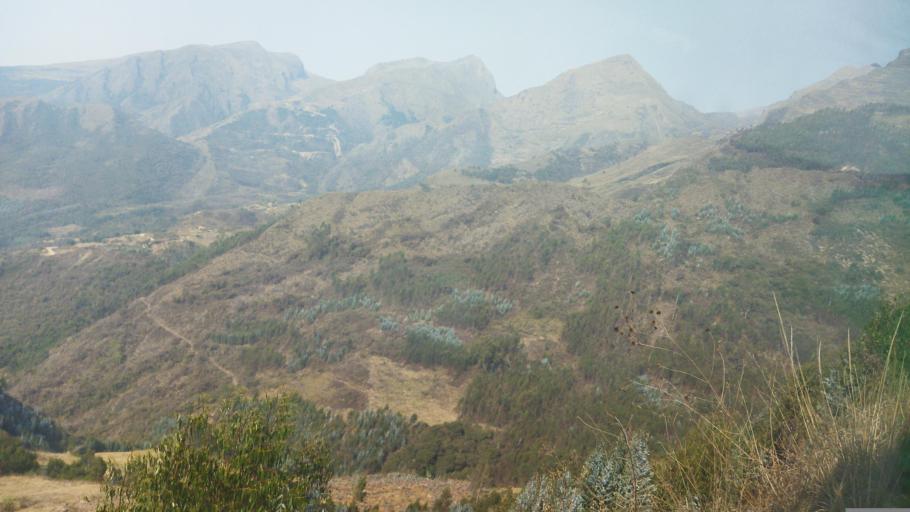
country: BO
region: La Paz
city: Quime
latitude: -16.9793
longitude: -67.1972
